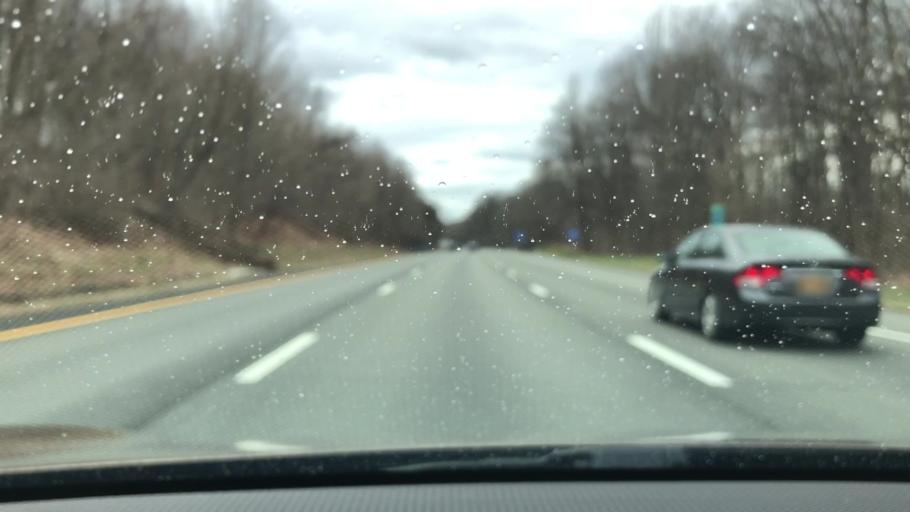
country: US
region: New Jersey
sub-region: Warren County
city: Belvidere
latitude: 40.9286
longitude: -75.0398
